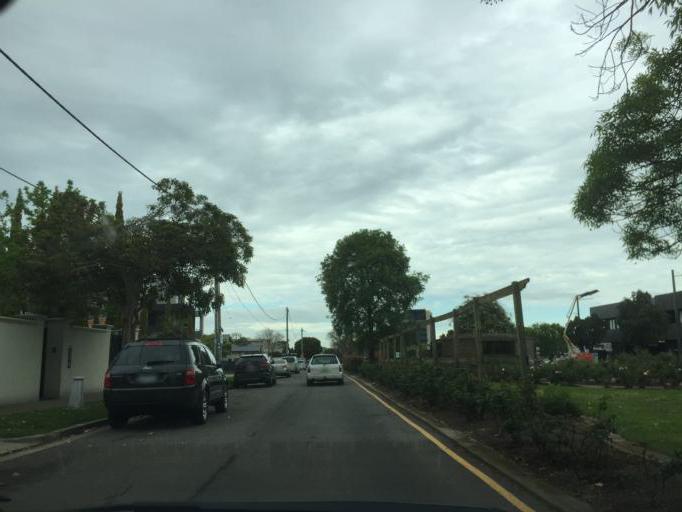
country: AU
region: Victoria
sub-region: Brimbank
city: Sunshine North
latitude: -37.7792
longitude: 144.8335
